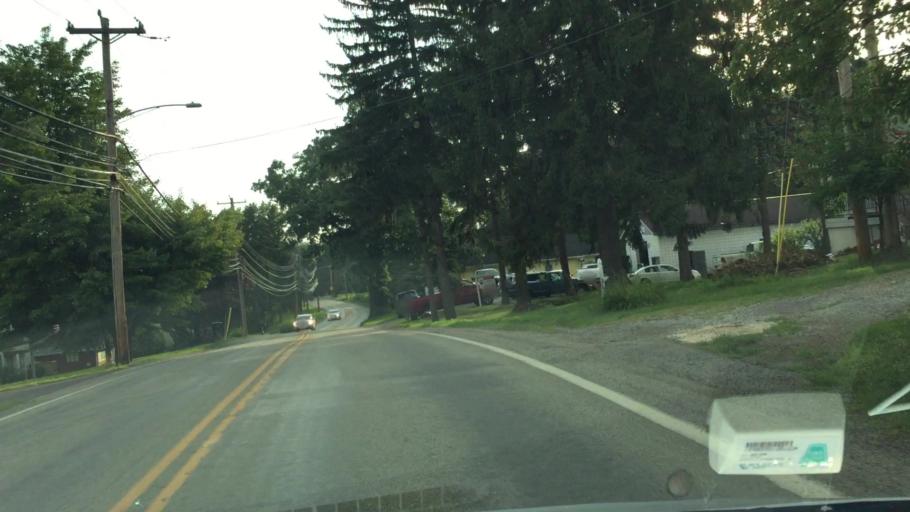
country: US
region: Pennsylvania
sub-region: Allegheny County
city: Carnot-Moon
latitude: 40.5104
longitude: -80.2349
